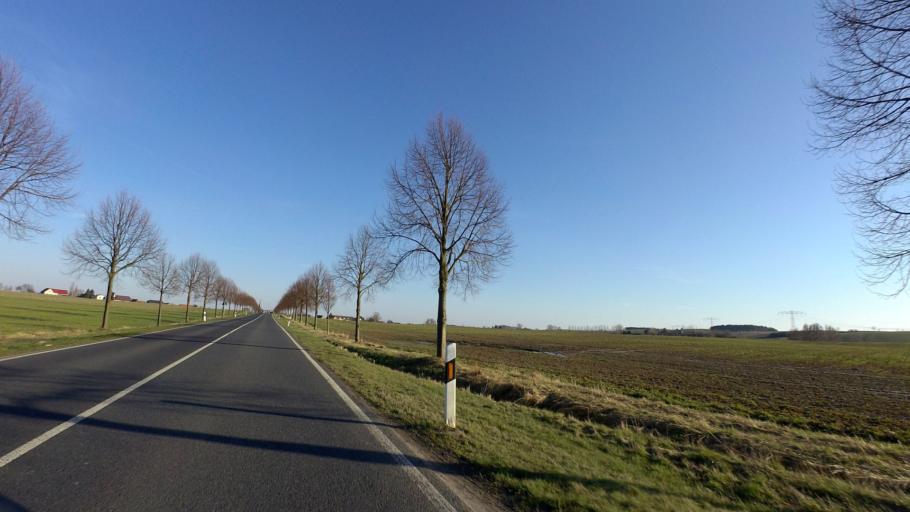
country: DE
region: Brandenburg
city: Britz
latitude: 52.9189
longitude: 13.7987
